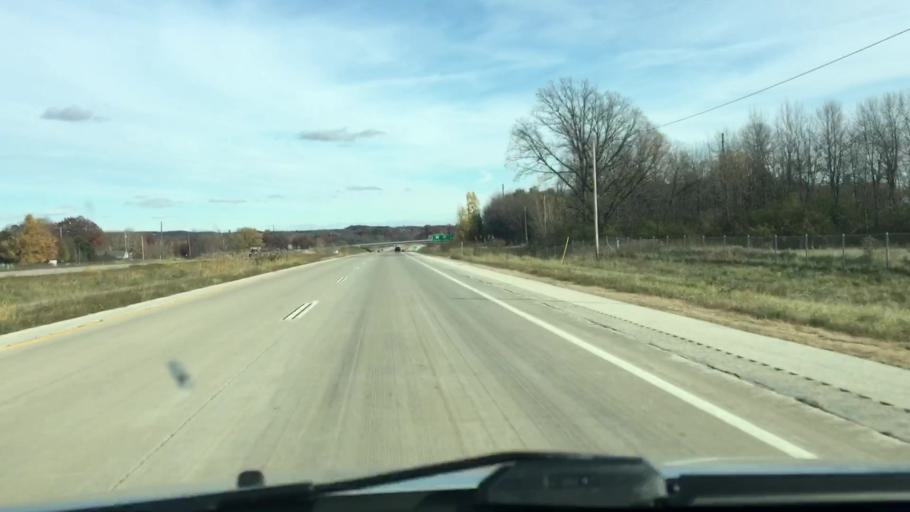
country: US
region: Wisconsin
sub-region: Kewaunee County
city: Luxemburg
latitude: 44.6339
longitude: -87.7858
